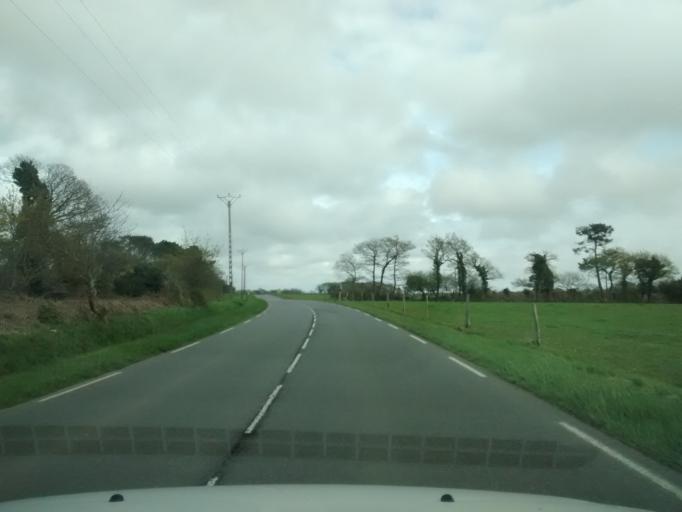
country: FR
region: Brittany
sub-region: Departement du Finistere
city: Clohars-Carnoet
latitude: 47.7979
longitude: -3.5477
